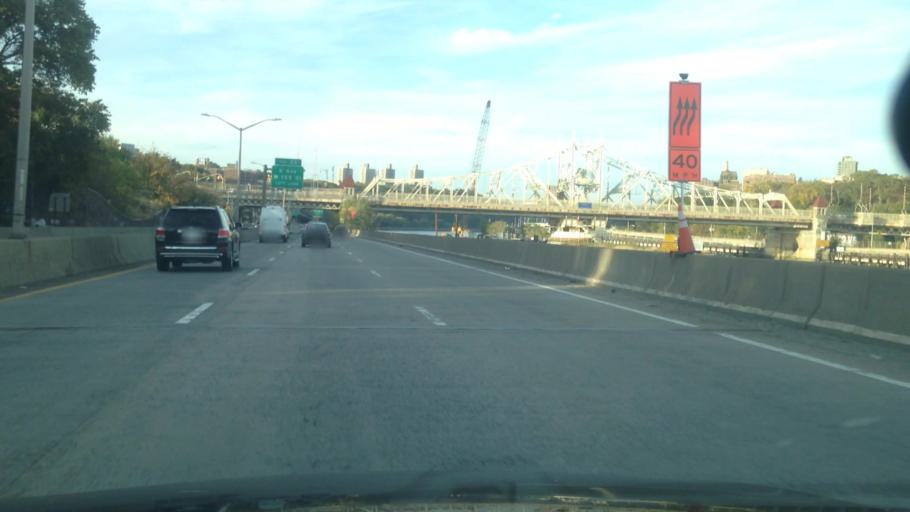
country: US
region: New York
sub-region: New York County
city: Inwood
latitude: 40.8258
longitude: -73.9344
